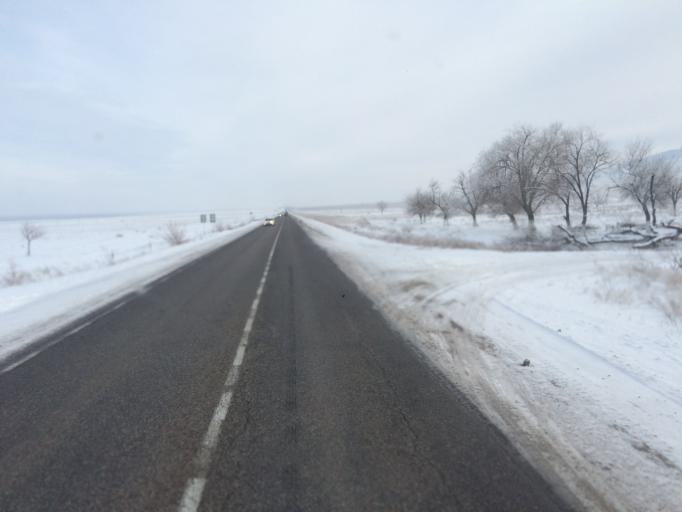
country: KG
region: Chuy
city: Ivanovka
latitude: 43.3792
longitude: 75.2197
